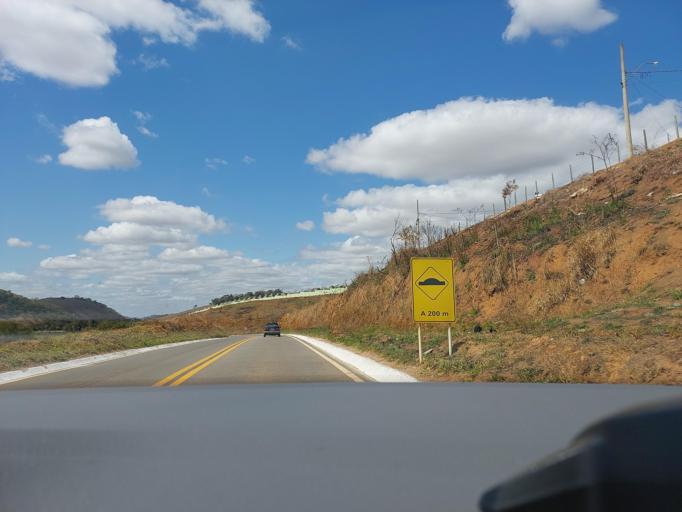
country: BR
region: Minas Gerais
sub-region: Muriae
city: Muriae
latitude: -21.1111
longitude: -42.4478
